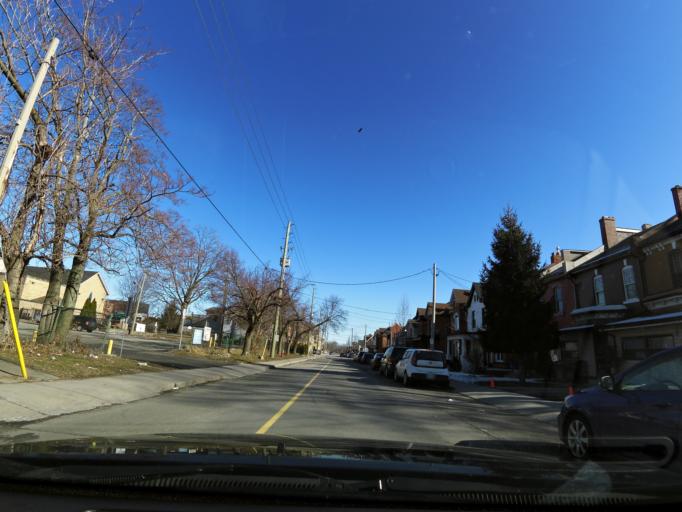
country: CA
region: Ontario
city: Hamilton
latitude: 43.2624
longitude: -79.8650
